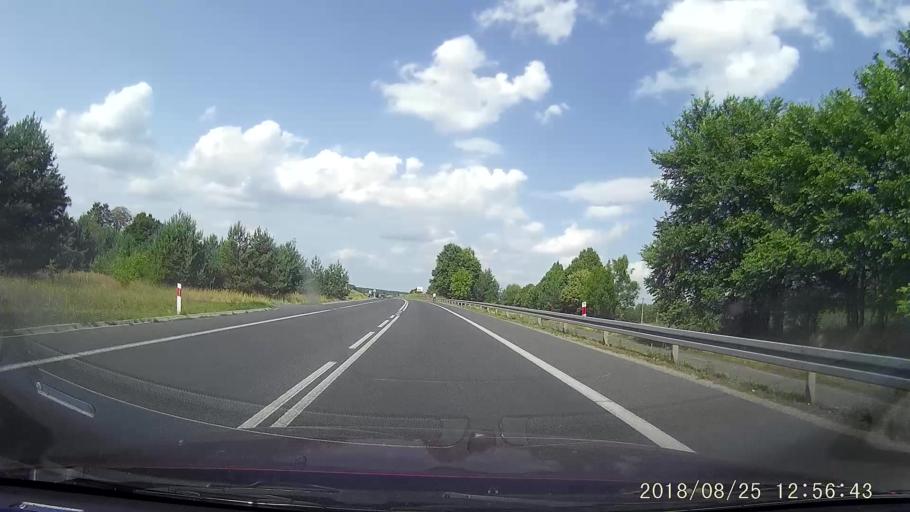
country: PL
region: West Pomeranian Voivodeship
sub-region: Powiat goleniowski
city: Przybiernow
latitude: 53.7436
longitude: 14.7757
